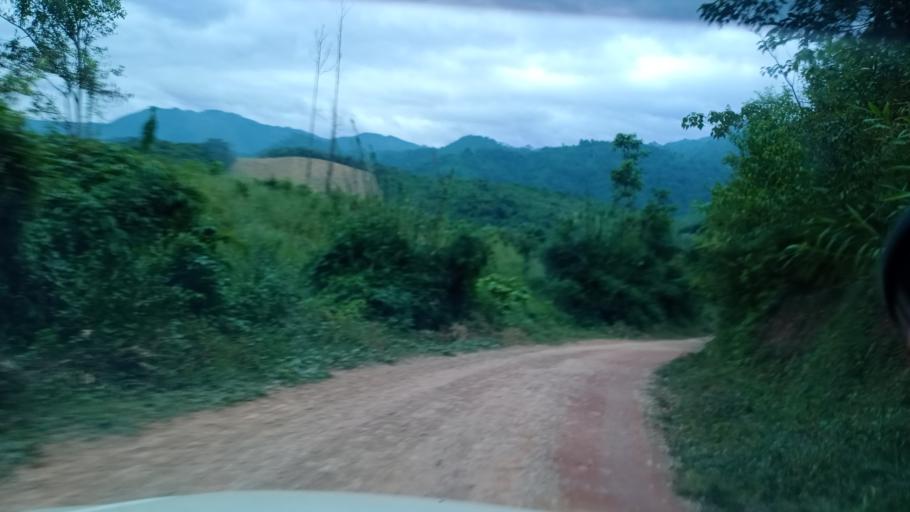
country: TH
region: Changwat Bueng Kan
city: Pak Khat
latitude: 18.7164
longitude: 103.2217
